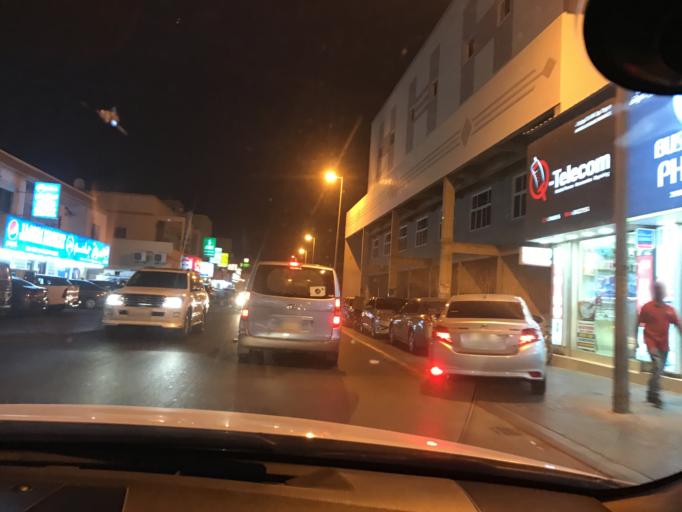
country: BH
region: Muharraq
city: Al Muharraq
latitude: 26.2718
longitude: 50.6073
